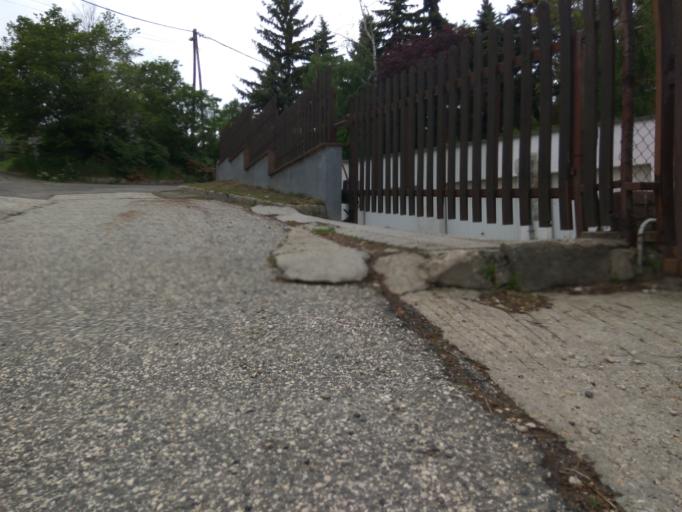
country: HU
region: Budapest
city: Budapest XII. keruelet
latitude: 47.4899
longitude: 18.9979
